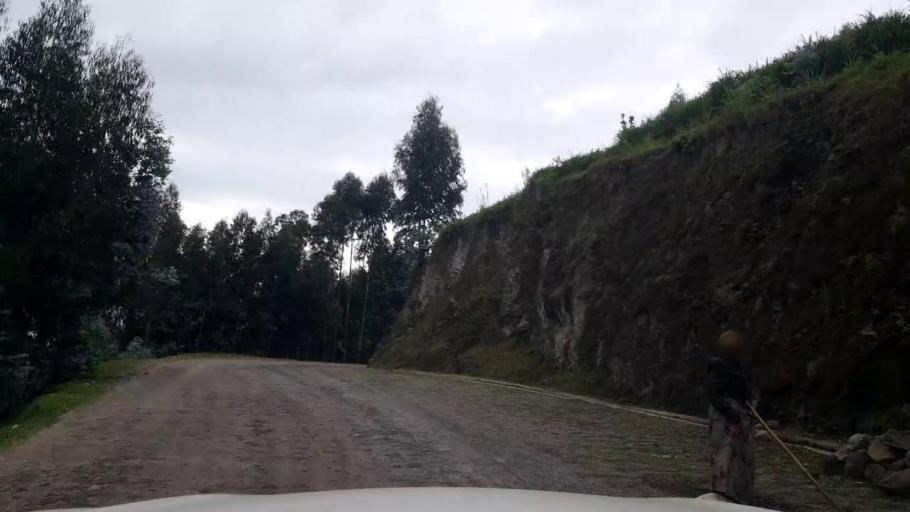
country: RW
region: Northern Province
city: Musanze
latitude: -1.5118
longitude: 29.5338
